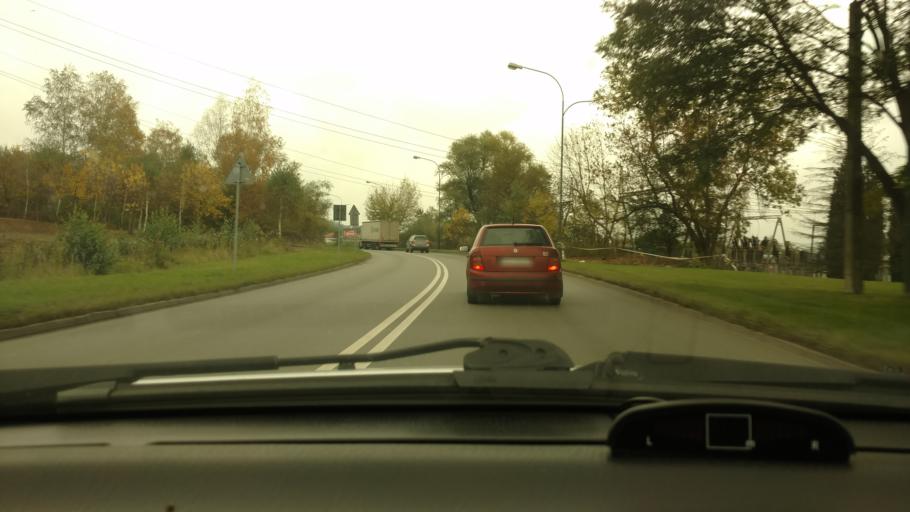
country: PL
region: Lesser Poland Voivodeship
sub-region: Powiat nowosadecki
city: Nowy Sacz
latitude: 49.6378
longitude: 20.6965
